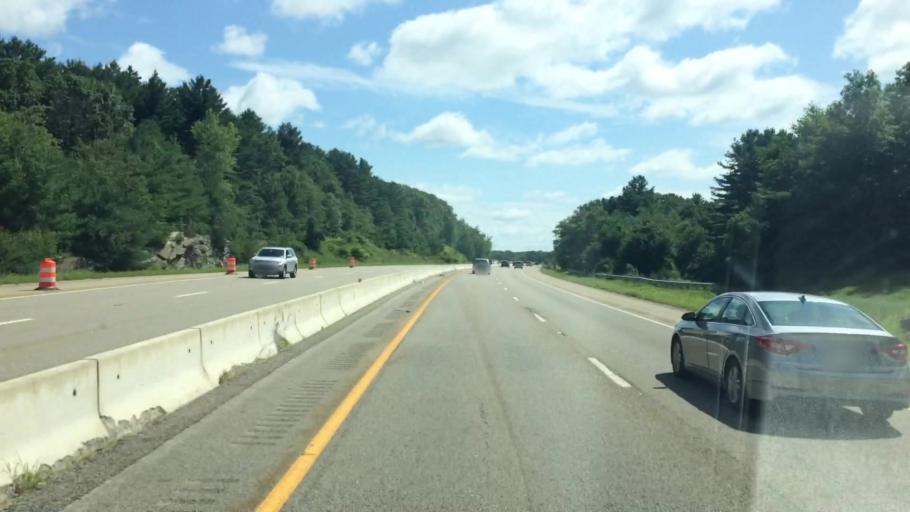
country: US
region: Rhode Island
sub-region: Providence County
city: Cumberland Hill
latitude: 41.9734
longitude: -71.4860
